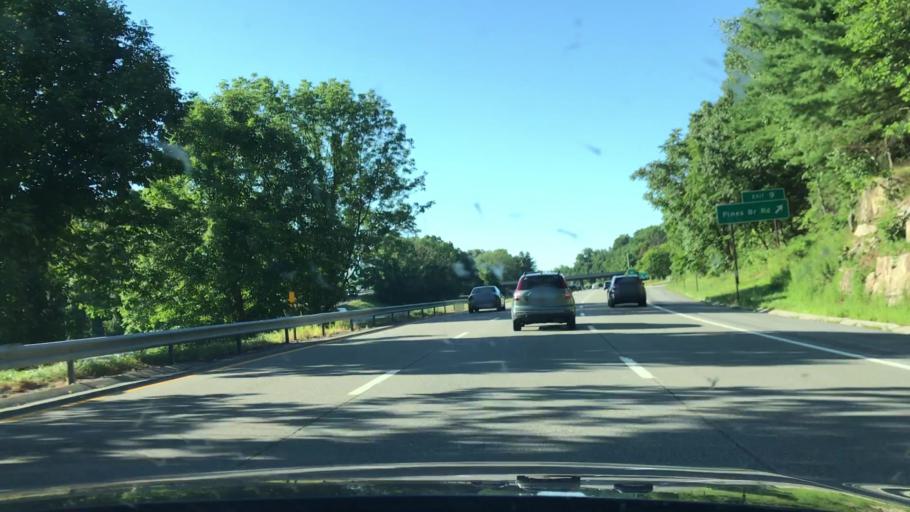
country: US
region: New York
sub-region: Westchester County
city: Briarcliff Manor
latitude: 41.1959
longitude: -73.8072
